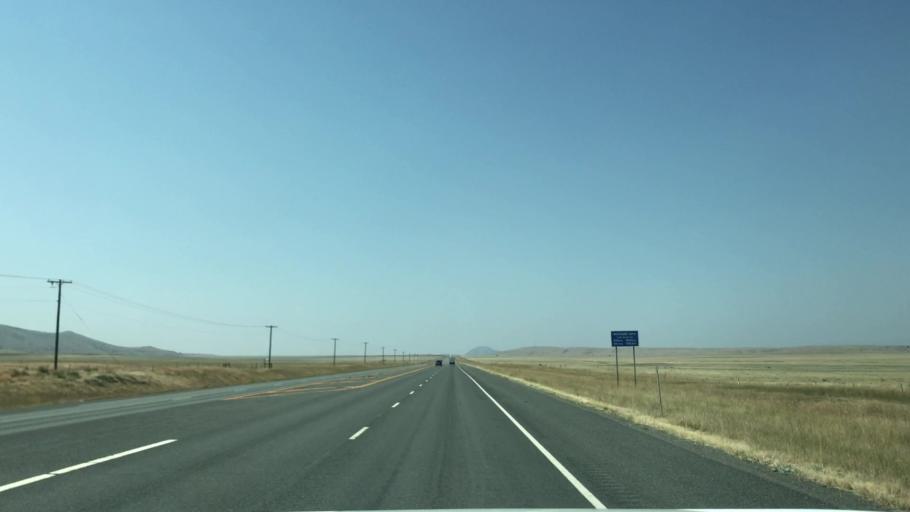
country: US
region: Montana
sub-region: Broadwater County
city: Townsend
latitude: 46.4184
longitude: -111.6030
